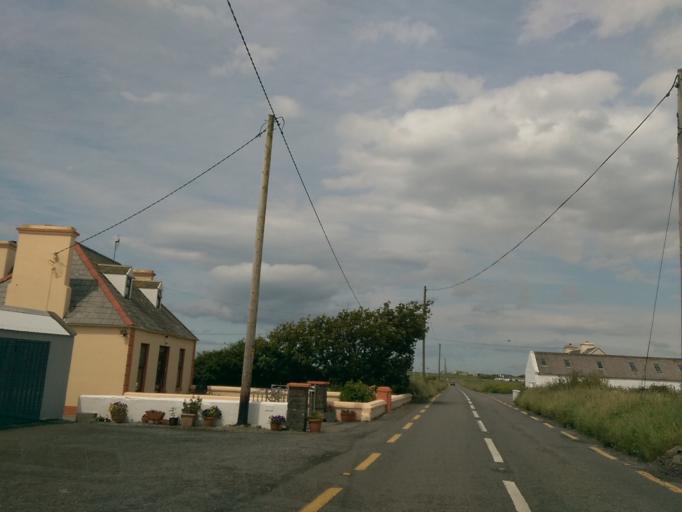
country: IE
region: Munster
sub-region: An Clar
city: Kilrush
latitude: 52.7552
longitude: -9.4771
